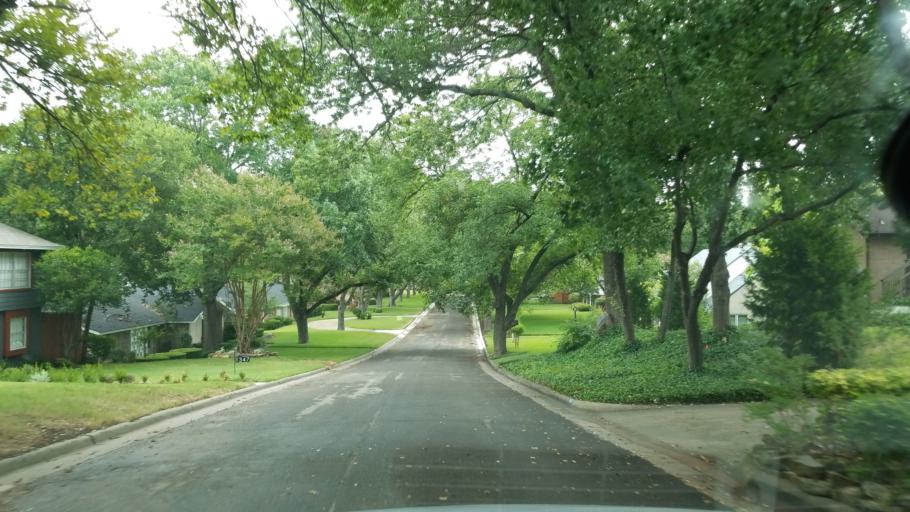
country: US
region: Texas
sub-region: Dallas County
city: Duncanville
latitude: 32.6708
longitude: -96.8428
